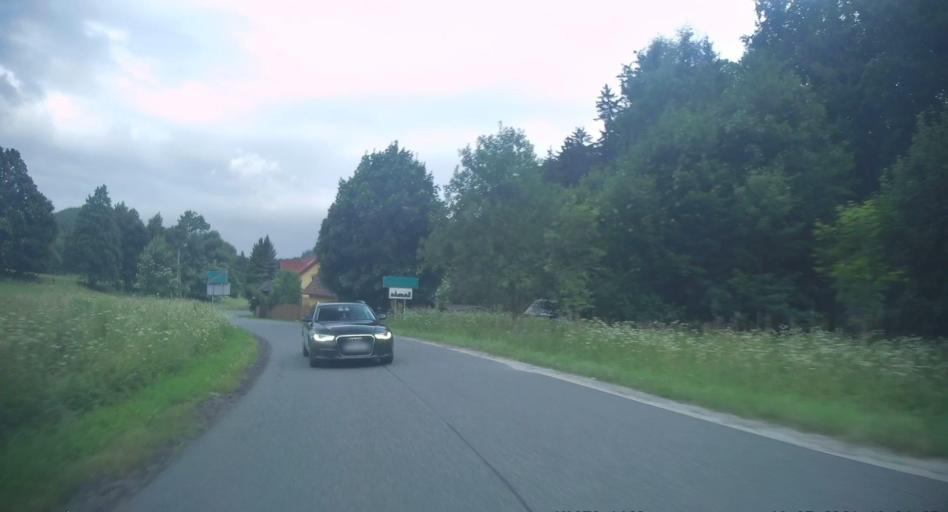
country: PL
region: Lower Silesian Voivodeship
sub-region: Powiat klodzki
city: Ludwikowice Klodzkie
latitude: 50.6481
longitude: 16.4737
